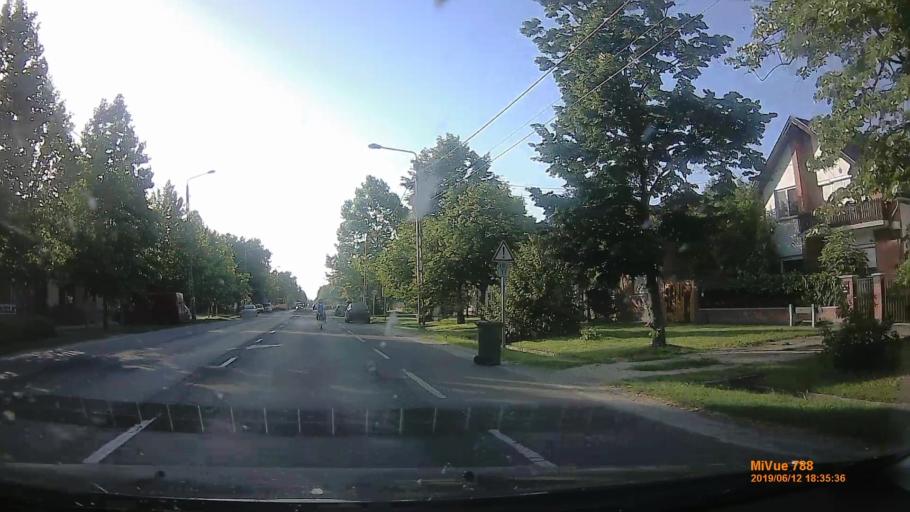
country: HU
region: Csongrad
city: Kistelek
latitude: 46.4671
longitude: 19.9828
